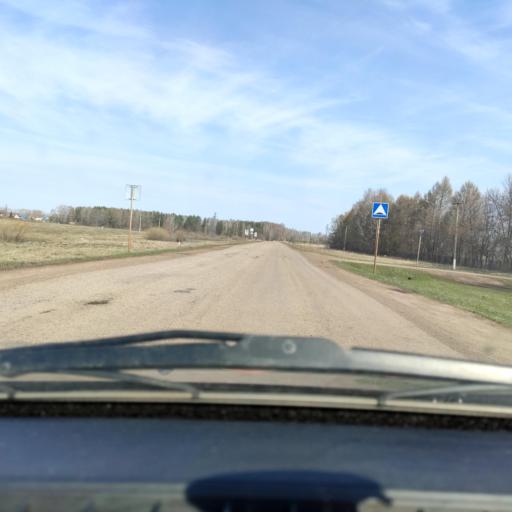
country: RU
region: Bashkortostan
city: Asanovo
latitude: 54.7673
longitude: 55.4870
